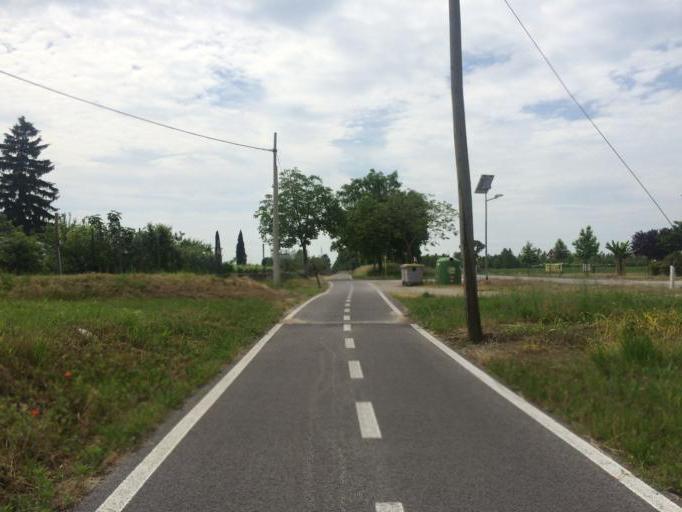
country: IT
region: Friuli Venezia Giulia
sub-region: Provincia di Udine
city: Aquileia
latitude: 45.7527
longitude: 13.3781
